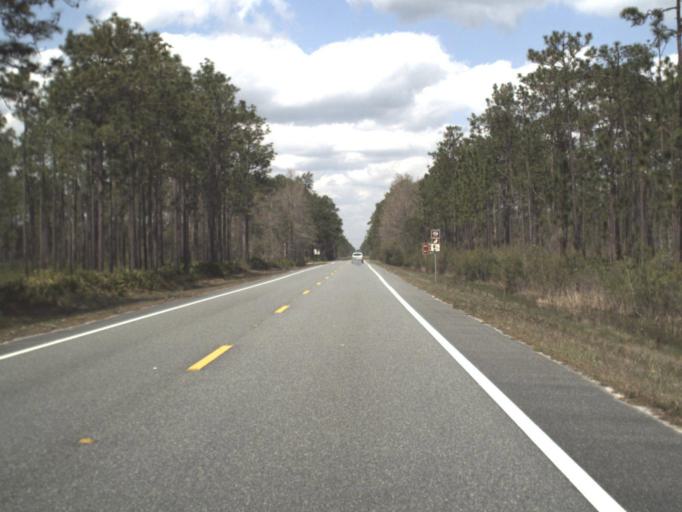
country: US
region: Florida
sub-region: Gulf County
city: Wewahitchka
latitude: 29.9902
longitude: -84.9765
